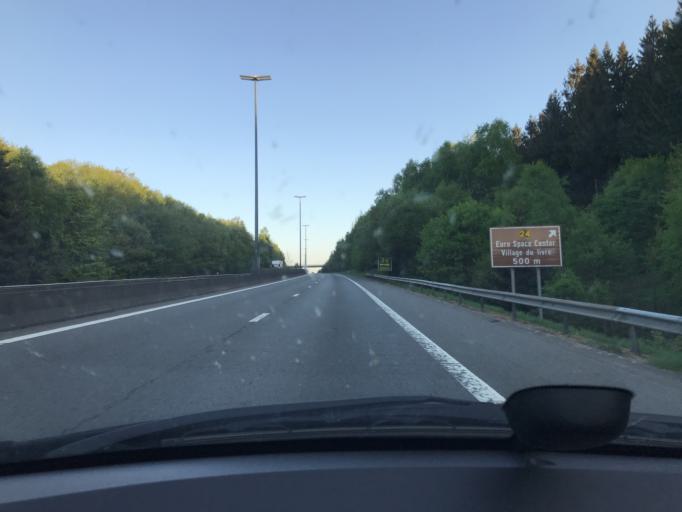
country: BE
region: Wallonia
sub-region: Province du Luxembourg
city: Libin
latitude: 50.0166
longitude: 5.2123
